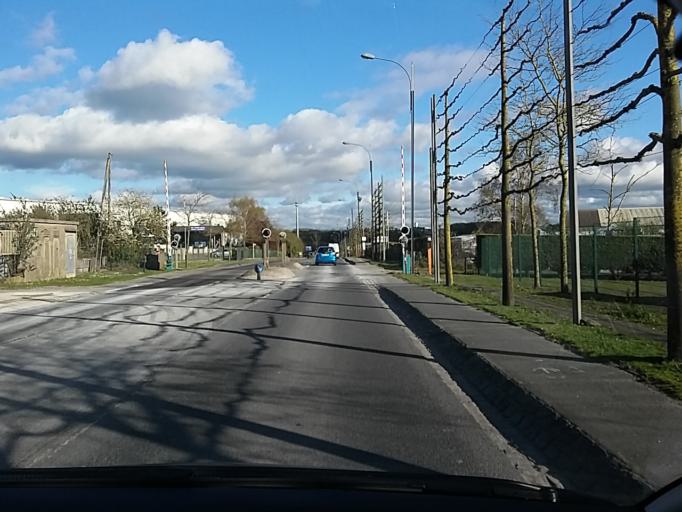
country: FR
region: Picardie
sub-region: Departement de la Somme
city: Amiens
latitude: 49.9292
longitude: 2.2814
